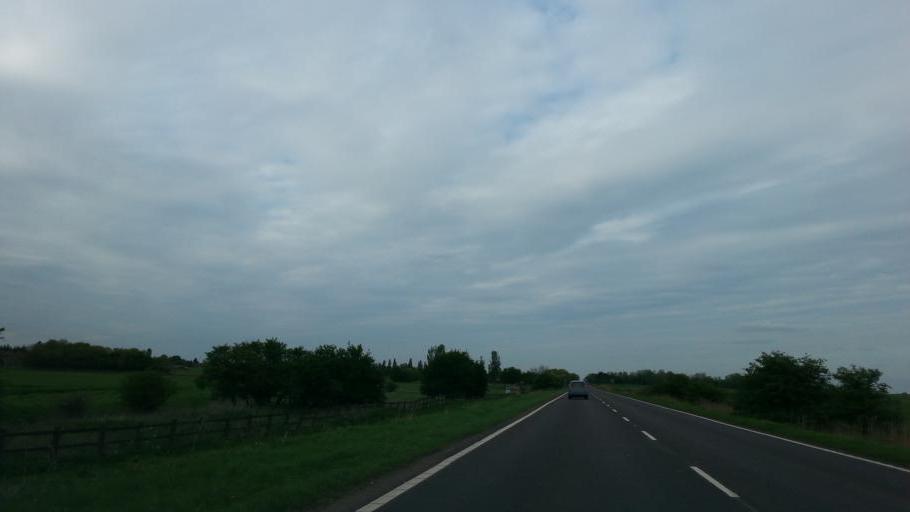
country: GB
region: England
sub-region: Cambridgeshire
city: Doddington
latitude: 52.4831
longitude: 0.0612
